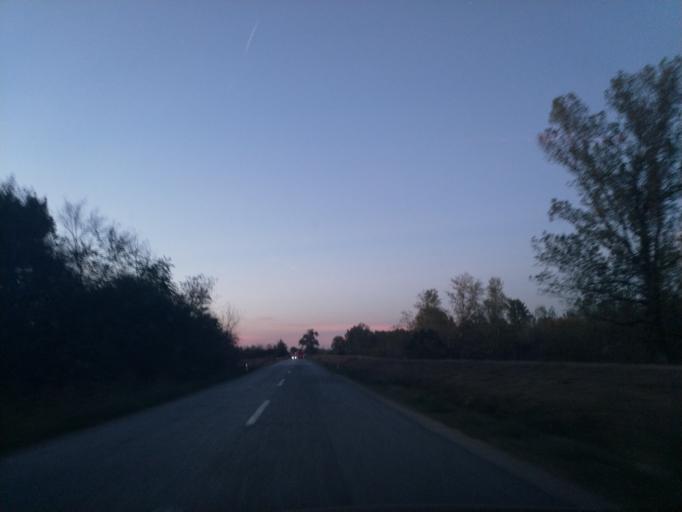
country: RS
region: Central Serbia
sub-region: Pomoravski Okrug
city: Svilajnac
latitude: 44.2253
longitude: 21.1478
